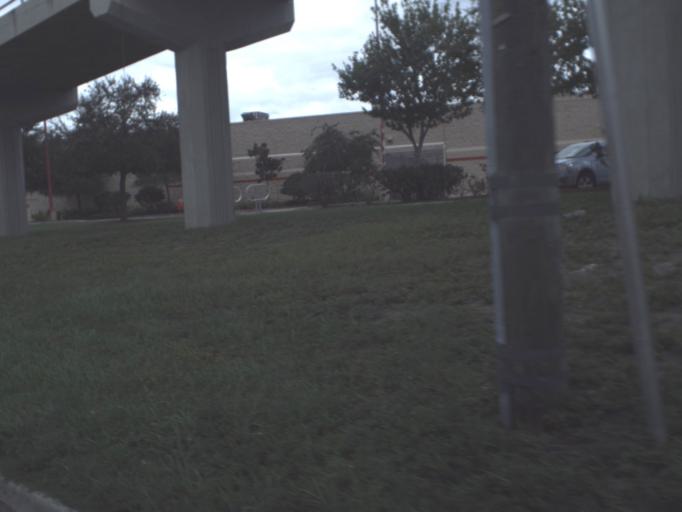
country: US
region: Florida
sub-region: Pinellas County
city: Bay Pines
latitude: 27.8109
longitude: -82.7561
